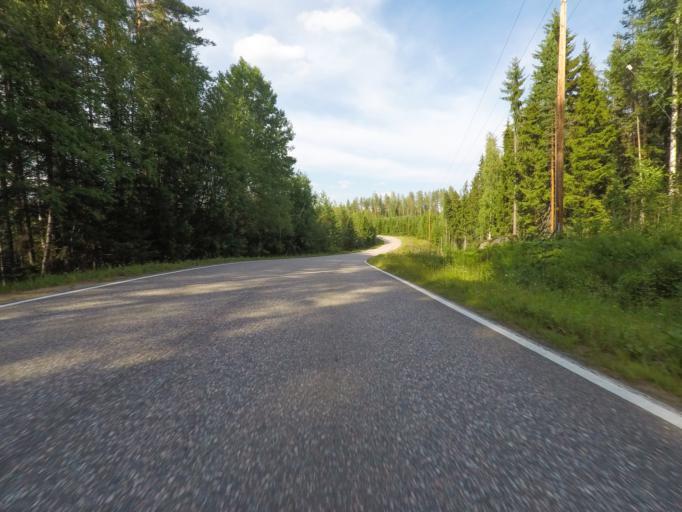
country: FI
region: Southern Savonia
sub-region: Savonlinna
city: Sulkava
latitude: 61.7694
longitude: 28.2361
